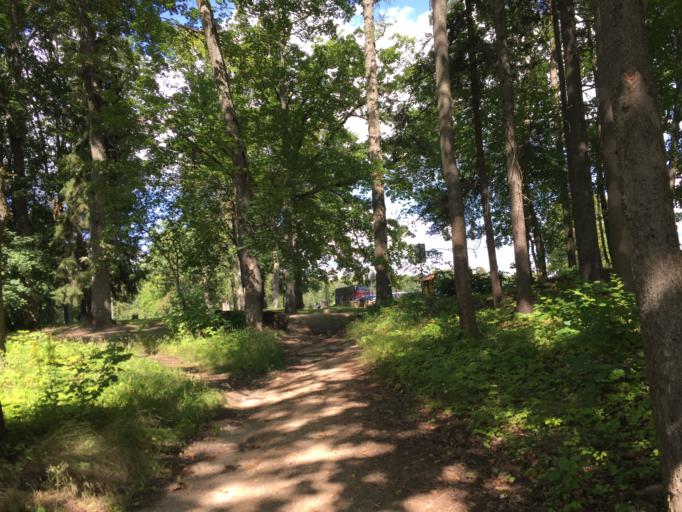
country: LV
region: Koknese
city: Koknese
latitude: 56.6385
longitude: 25.4229
